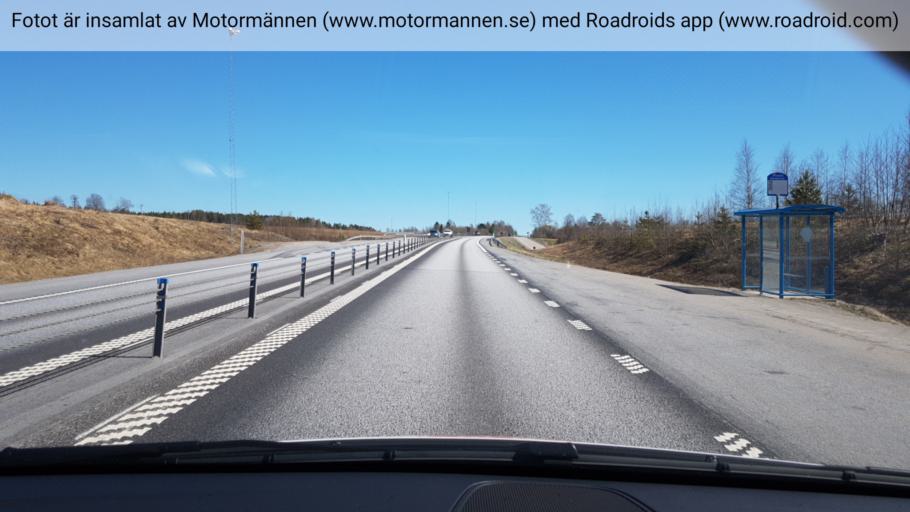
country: SE
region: Vaesterbotten
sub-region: Umea Kommun
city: Roback
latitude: 63.8847
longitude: 20.0326
